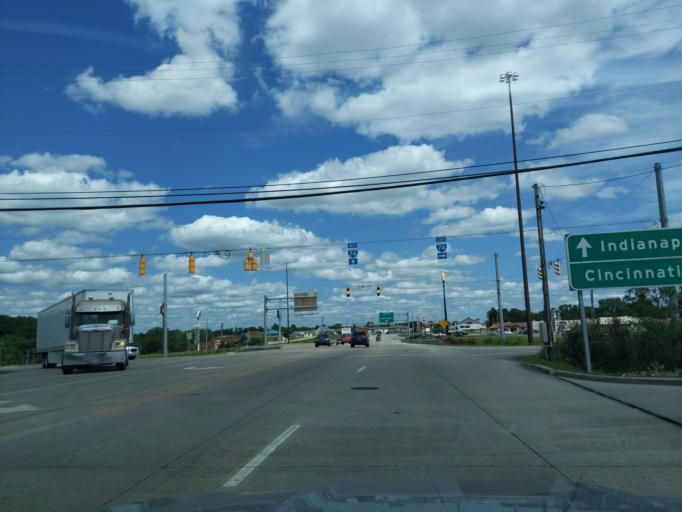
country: US
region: Indiana
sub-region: Ripley County
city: Batesville
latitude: 39.3070
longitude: -85.2173
